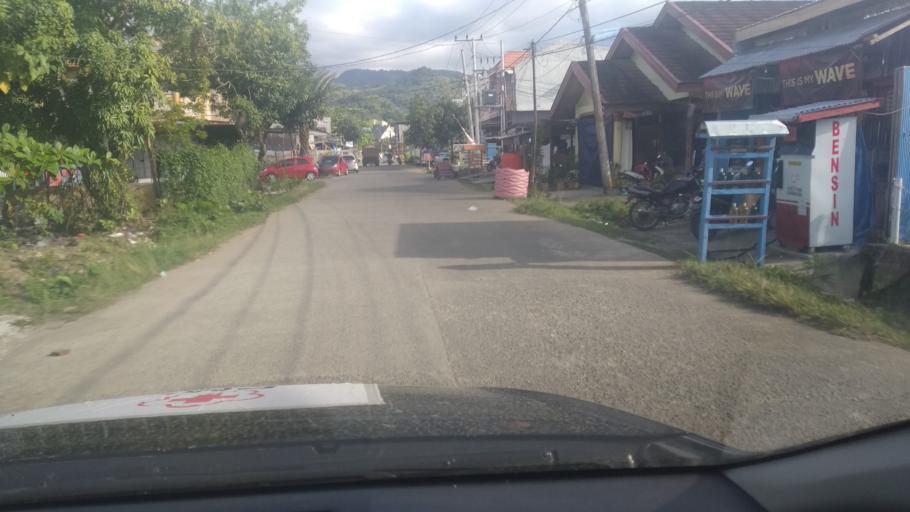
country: ID
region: Sulawesi Barat
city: Mamuju
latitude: -2.6788
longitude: 118.8857
